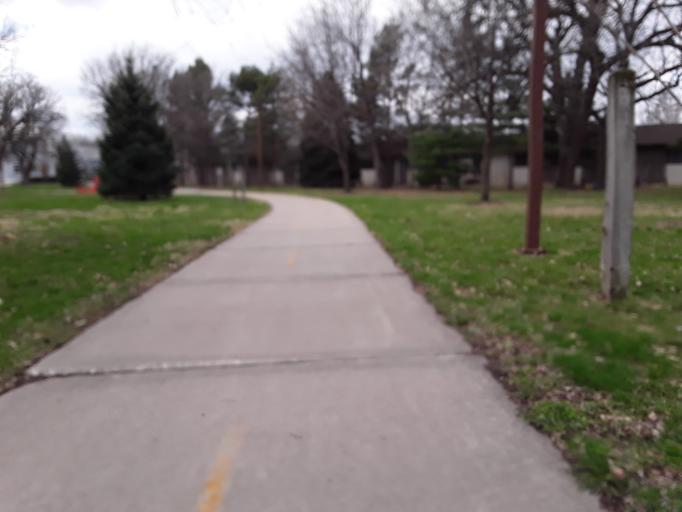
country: US
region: Nebraska
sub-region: Lancaster County
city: Lincoln
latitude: 40.8291
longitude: -96.6912
